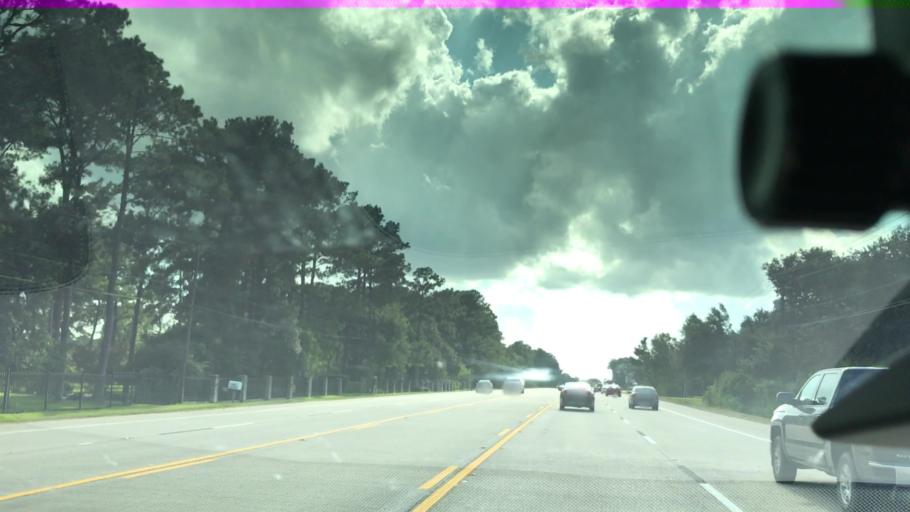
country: US
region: Texas
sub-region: Harris County
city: Webster
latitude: 29.4937
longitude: -95.1443
